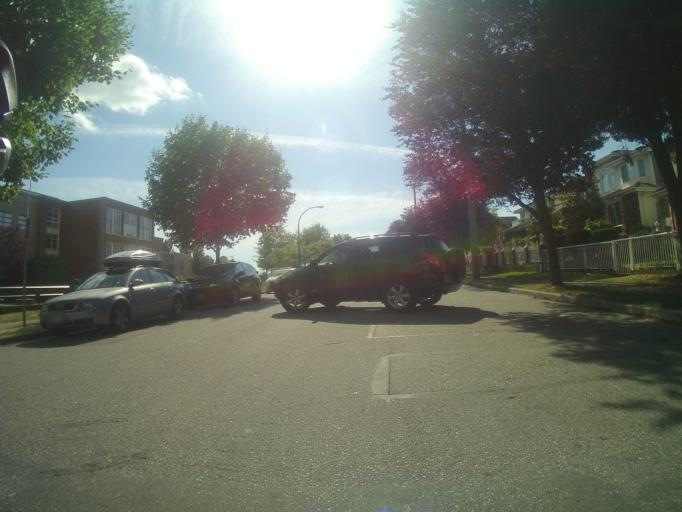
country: CA
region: British Columbia
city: Vancouver
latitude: 49.2165
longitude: -123.0835
